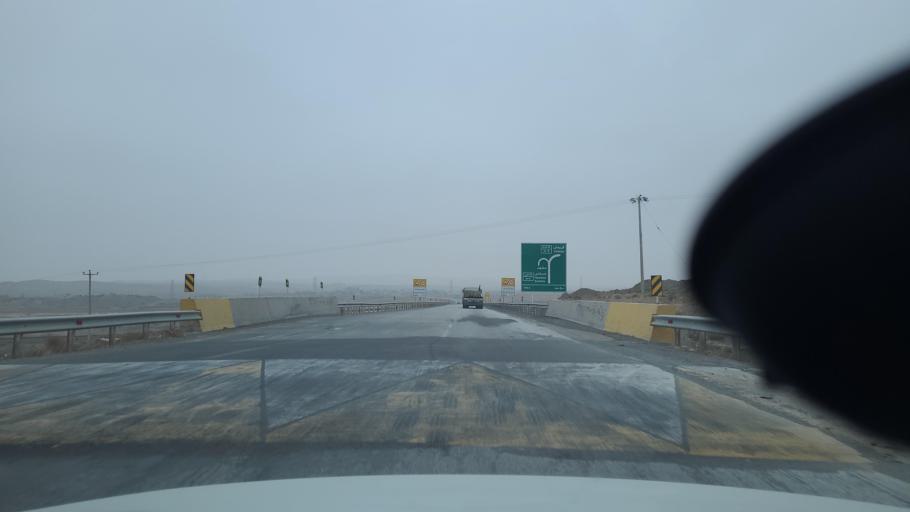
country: IR
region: Razavi Khorasan
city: Fariman
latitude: 35.9862
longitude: 59.7424
